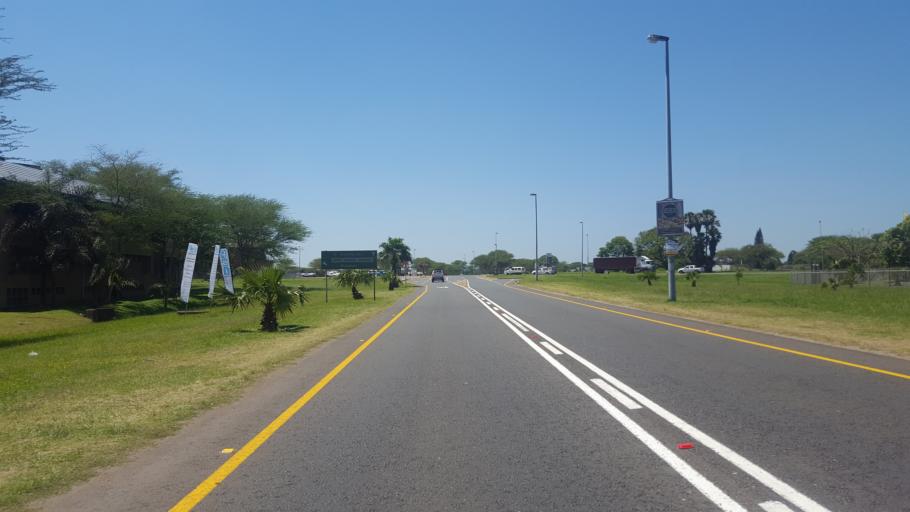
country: ZA
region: KwaZulu-Natal
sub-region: uThungulu District Municipality
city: Richards Bay
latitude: -28.7521
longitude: 32.0548
